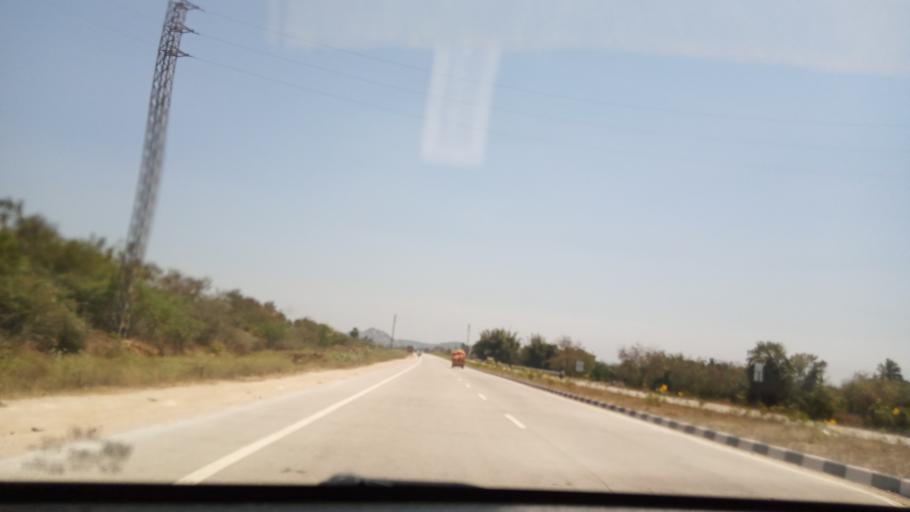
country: IN
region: Andhra Pradesh
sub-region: Chittoor
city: Chittoor
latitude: 13.1942
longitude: 79.0256
